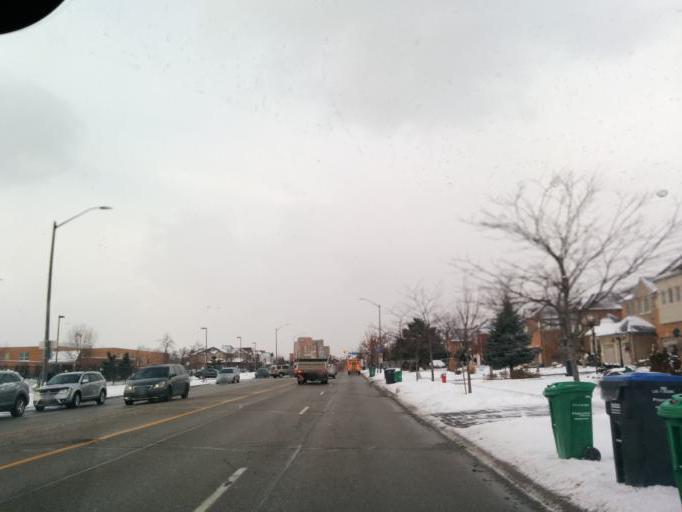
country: CA
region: Ontario
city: Mississauga
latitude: 43.5689
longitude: -79.7317
